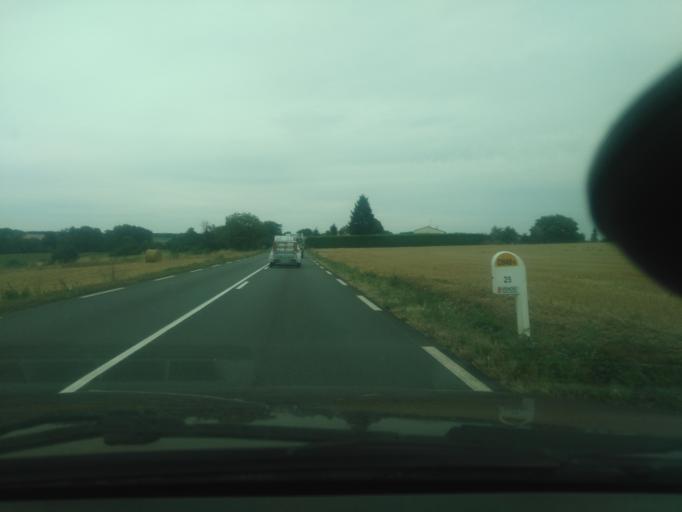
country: FR
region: Pays de la Loire
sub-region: Departement de la Vendee
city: Bazoges-en-Pareds
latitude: 46.6799
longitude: -0.9573
